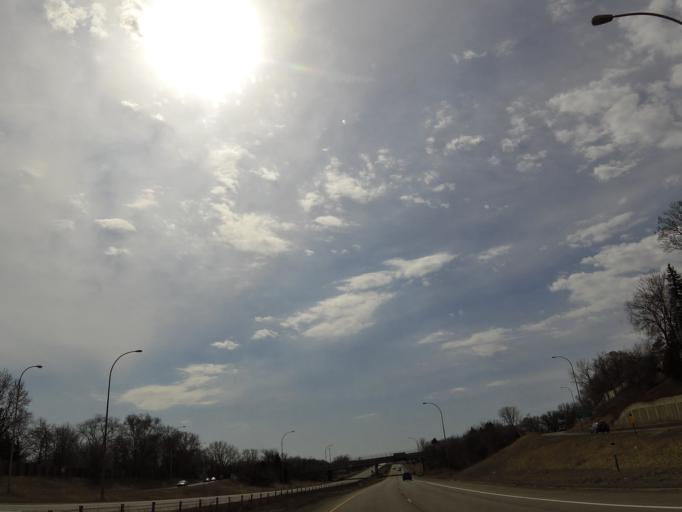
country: US
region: Minnesota
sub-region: Dakota County
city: South Saint Paul
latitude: 44.9040
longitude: -93.0651
